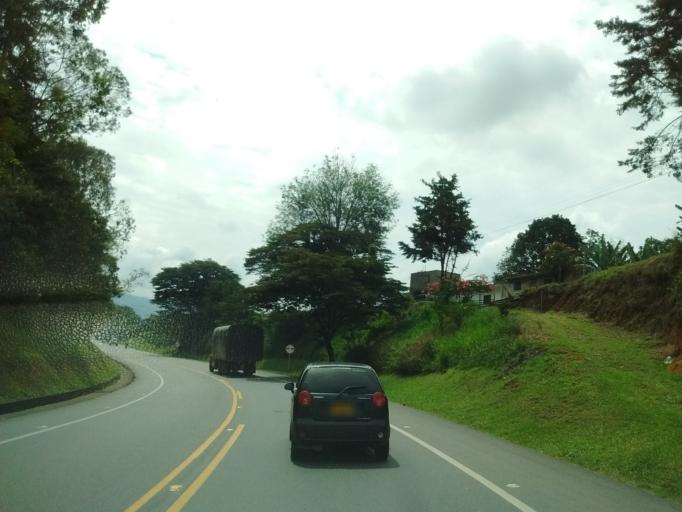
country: CO
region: Cauca
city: Morales
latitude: 2.7547
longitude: -76.5543
